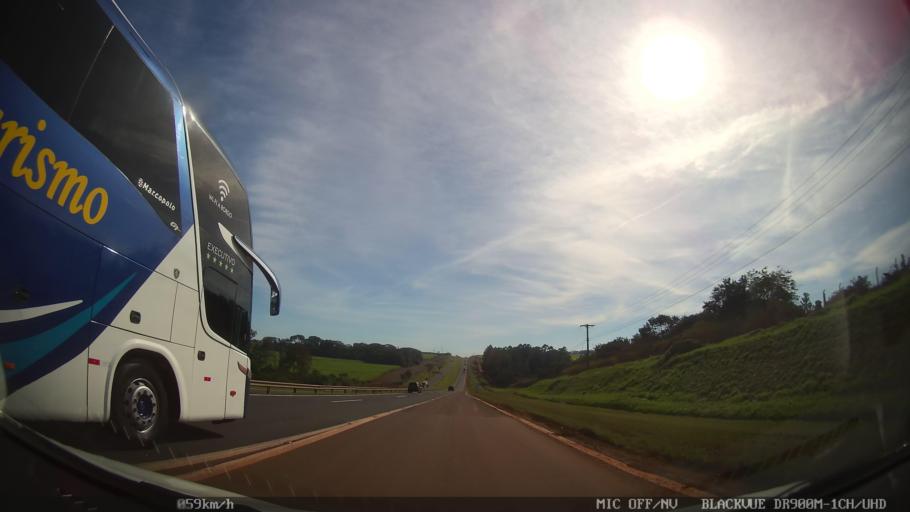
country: BR
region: Sao Paulo
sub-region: Araras
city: Araras
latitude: -22.3105
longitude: -47.3910
